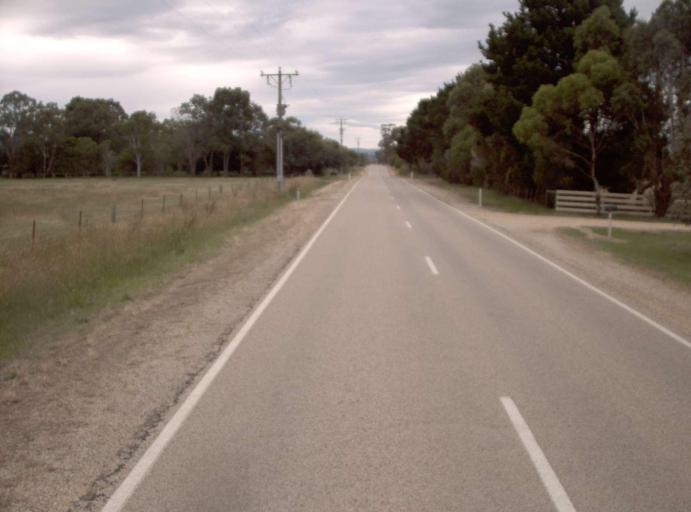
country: AU
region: Victoria
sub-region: East Gippsland
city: Bairnsdale
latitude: -37.8585
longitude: 147.5639
